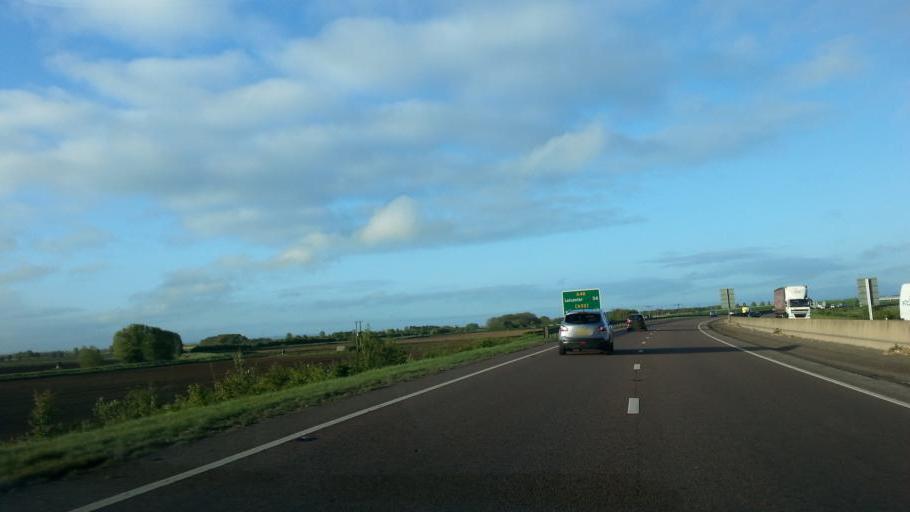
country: GB
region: England
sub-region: Nottinghamshire
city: Farndon
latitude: 53.0604
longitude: -0.8368
